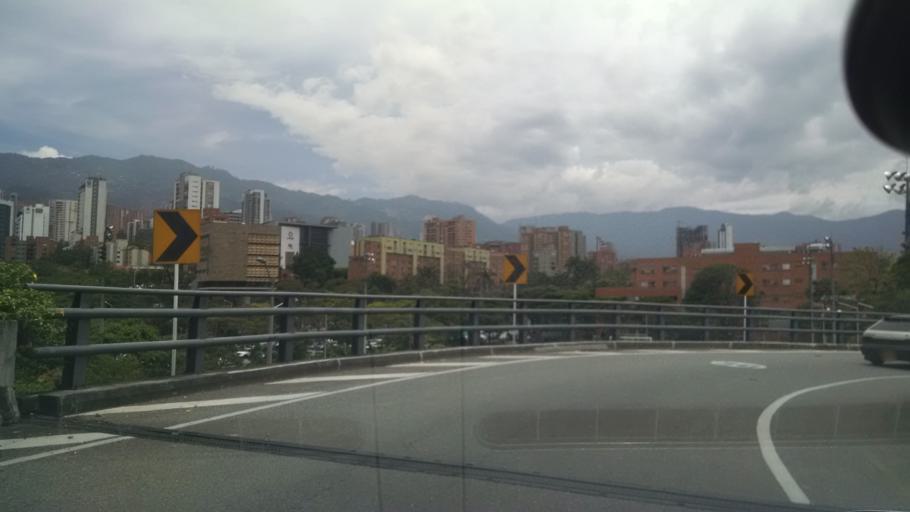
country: CO
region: Antioquia
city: Itagui
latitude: 6.2034
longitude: -75.5785
